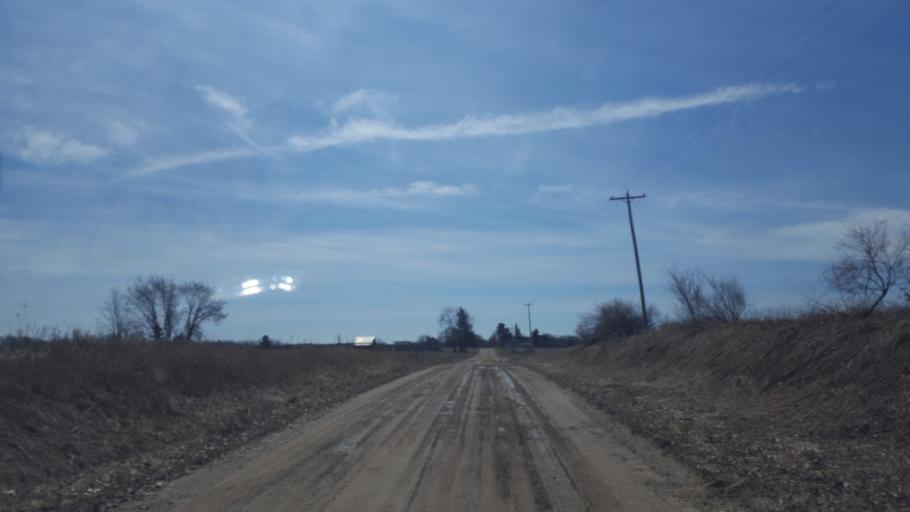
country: US
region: Michigan
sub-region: Montcalm County
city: Edmore
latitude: 43.4995
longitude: -85.0454
